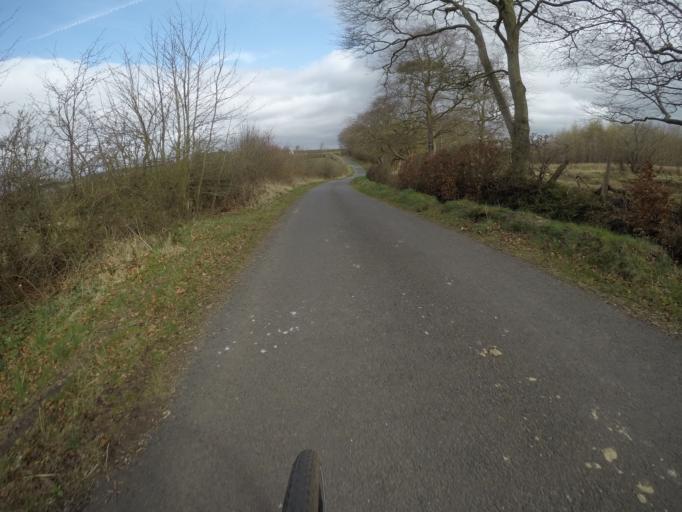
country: GB
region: Scotland
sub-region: North Ayrshire
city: Springside
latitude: 55.6542
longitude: -4.6114
